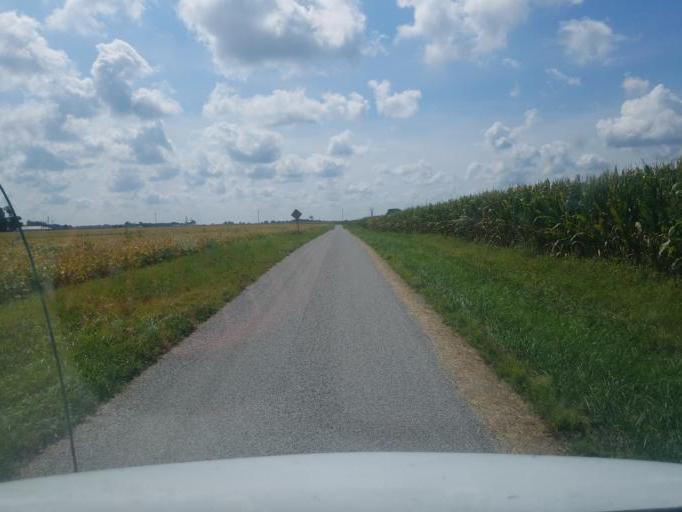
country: US
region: Ohio
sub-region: Marion County
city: Prospect
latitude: 40.4757
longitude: -83.1420
